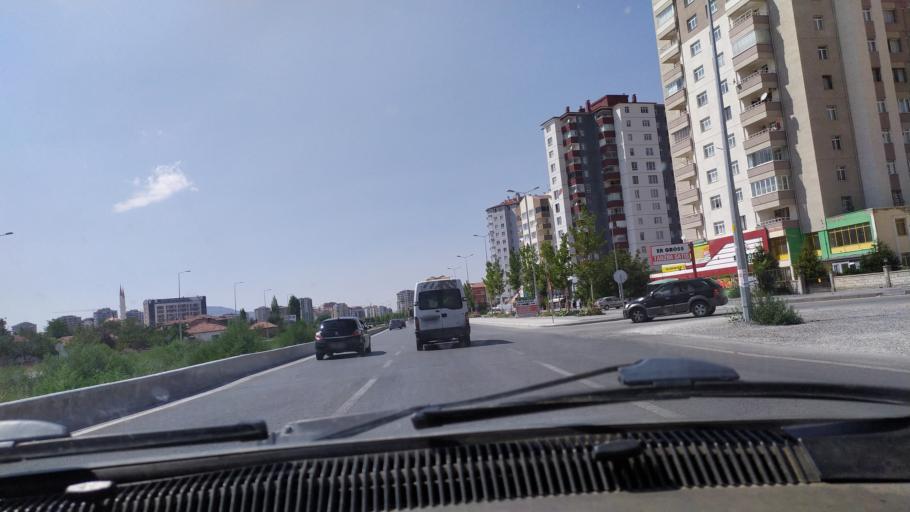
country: TR
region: Kayseri
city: Talas
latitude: 38.7220
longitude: 35.5330
